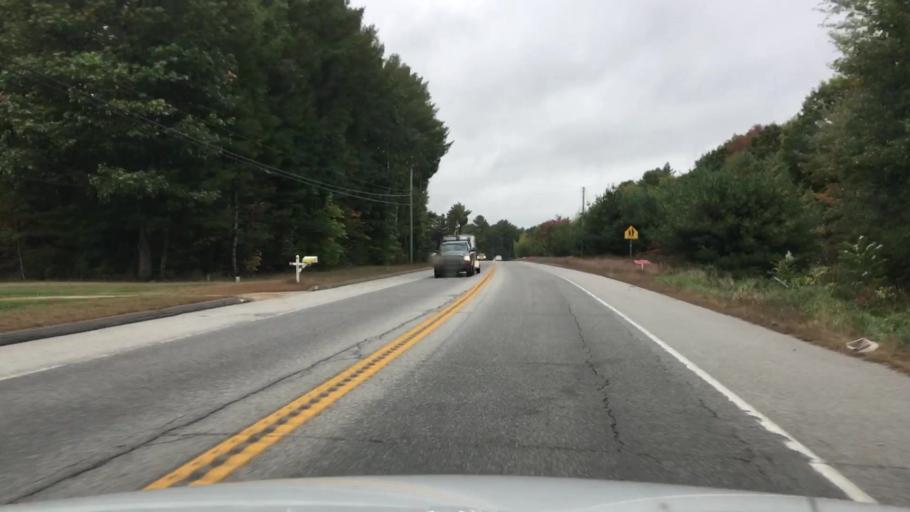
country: US
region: Maine
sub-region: Oxford County
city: Oxford
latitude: 44.1661
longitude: -70.5021
